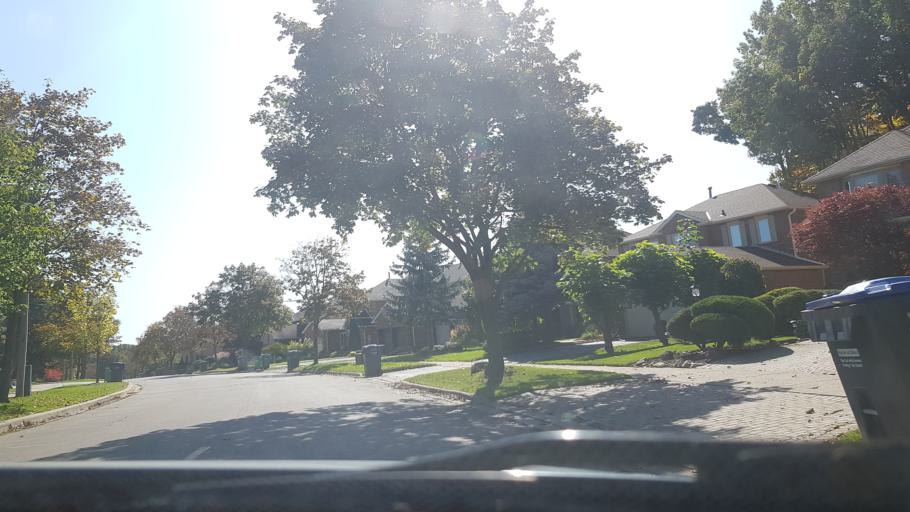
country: CA
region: Ontario
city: Brampton
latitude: 43.7432
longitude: -79.8054
